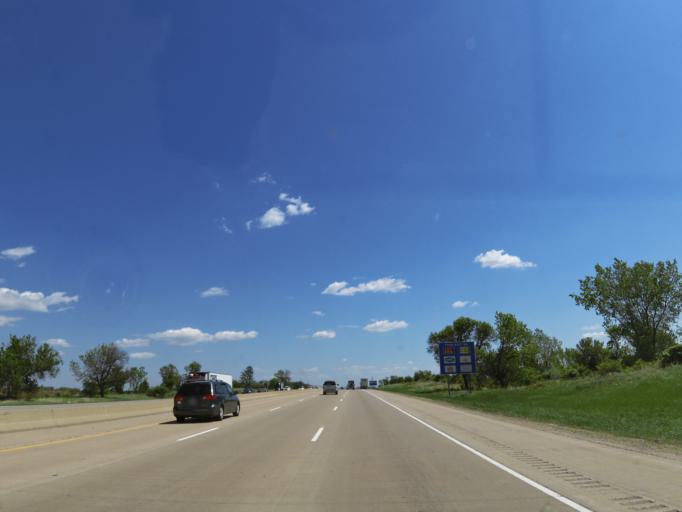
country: US
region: Wisconsin
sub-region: Dane County
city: De Forest
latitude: 43.2647
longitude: -89.3891
